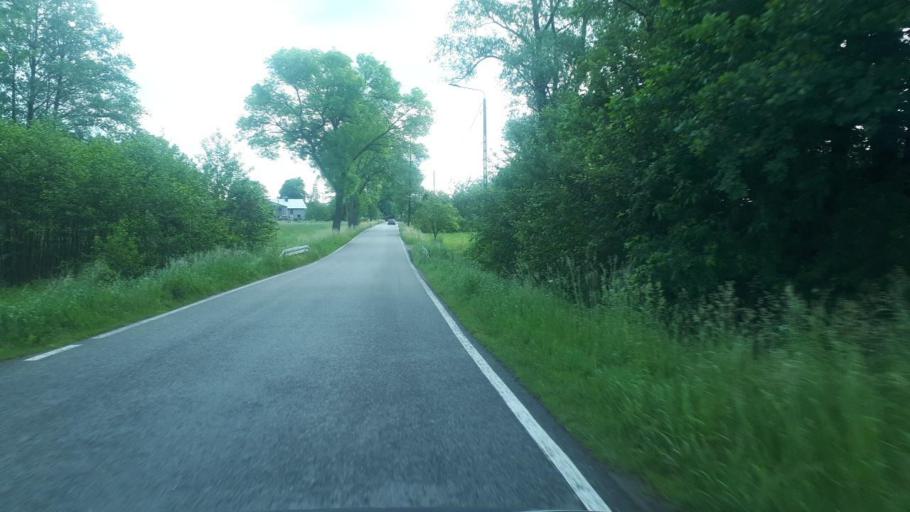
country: PL
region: Silesian Voivodeship
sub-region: Powiat bielski
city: Kaniow
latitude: 49.9531
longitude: 19.0230
